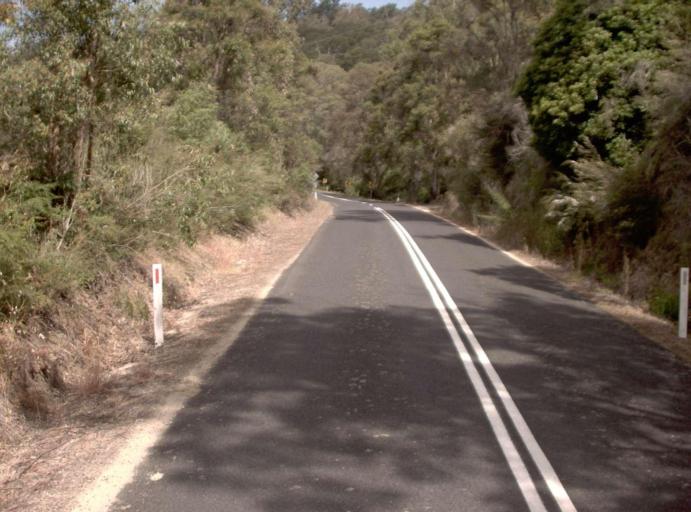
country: AU
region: New South Wales
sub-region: Bega Valley
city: Eden
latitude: -37.4812
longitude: 149.6001
